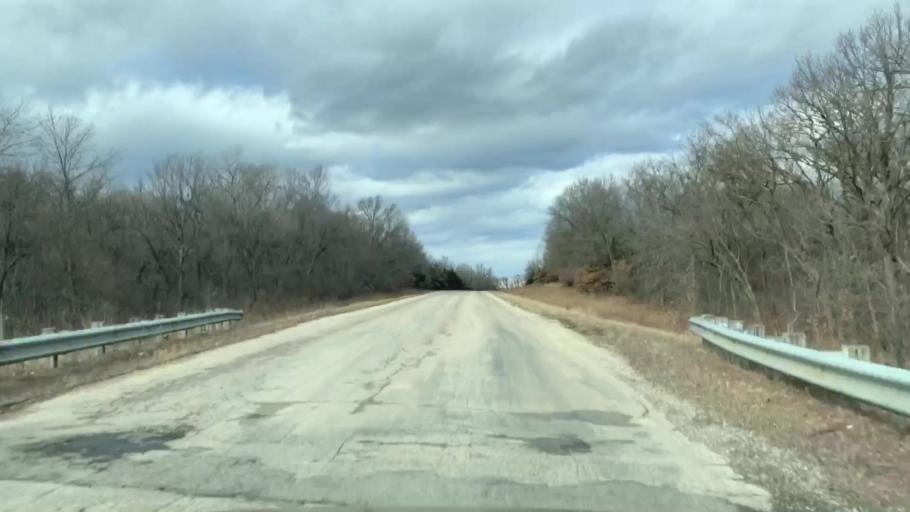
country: US
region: Kansas
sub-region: Allen County
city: Humboldt
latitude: 37.7534
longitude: -95.4712
